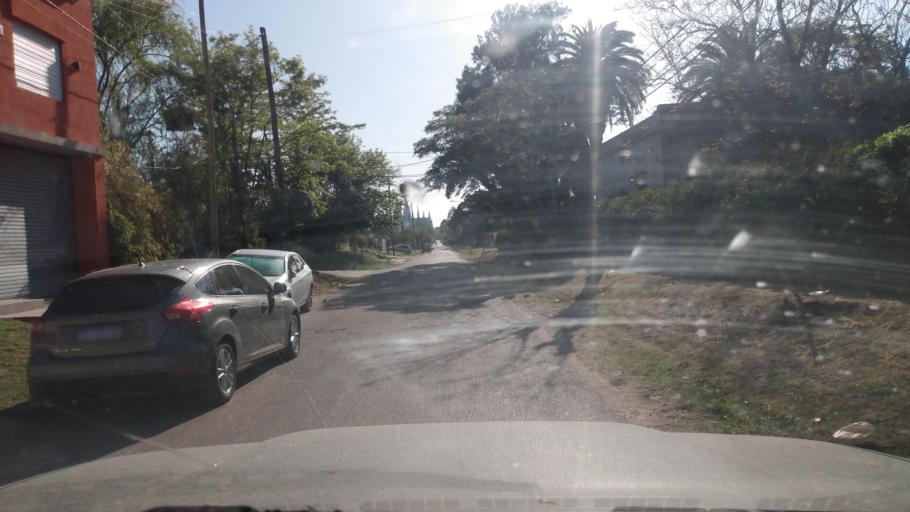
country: AR
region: Buenos Aires
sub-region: Partido de Lujan
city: Lujan
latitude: -34.5716
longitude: -59.1341
